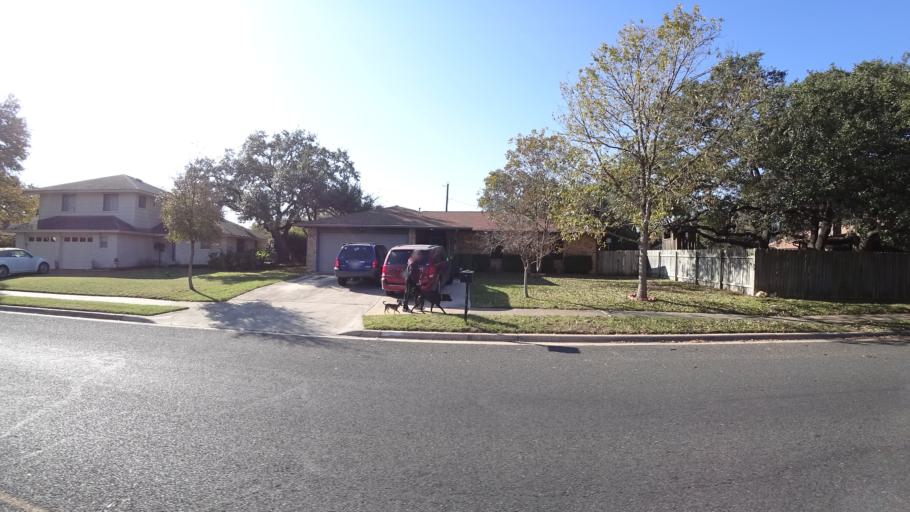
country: US
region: Texas
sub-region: Travis County
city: Barton Creek
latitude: 30.2289
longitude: -97.8454
